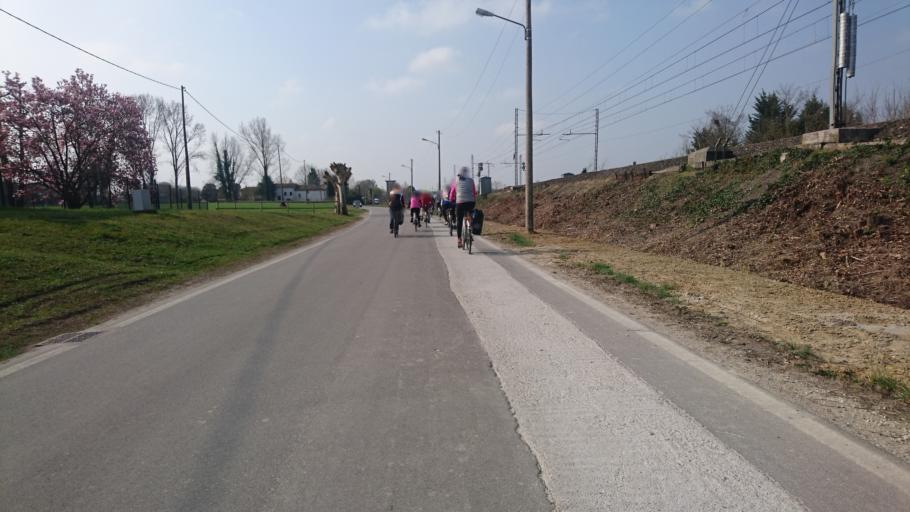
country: IT
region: Veneto
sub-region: Provincia di Padova
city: Mandriola-Sant'Agostino
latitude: 45.3852
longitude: 11.8351
